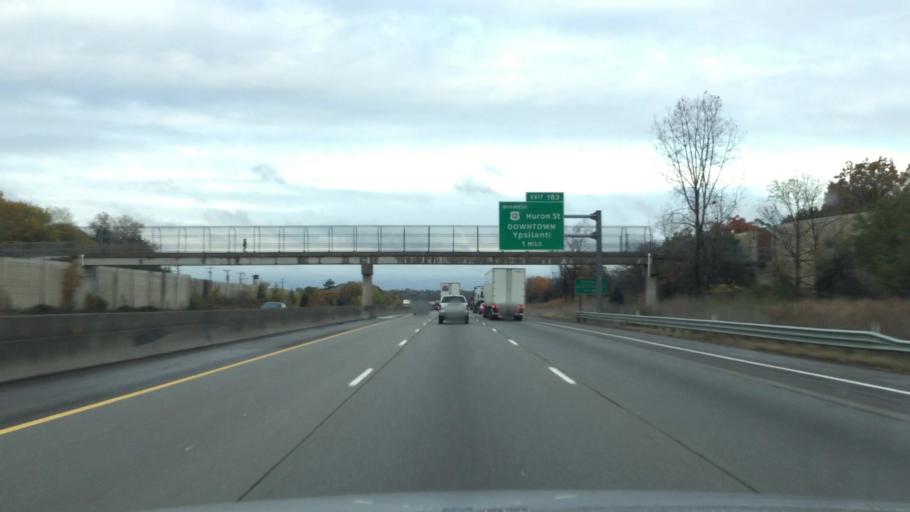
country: US
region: Michigan
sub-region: Washtenaw County
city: Ypsilanti
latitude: 42.2318
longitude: -83.5897
